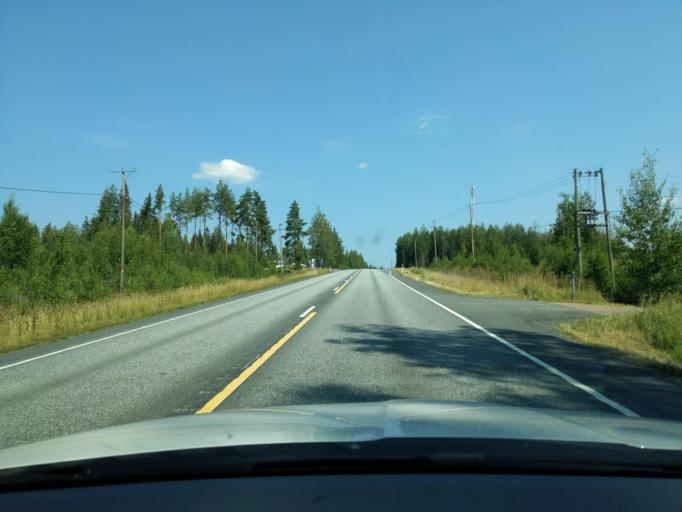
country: FI
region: Haeme
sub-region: Forssa
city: Ypaejae
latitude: 60.7652
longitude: 23.3226
